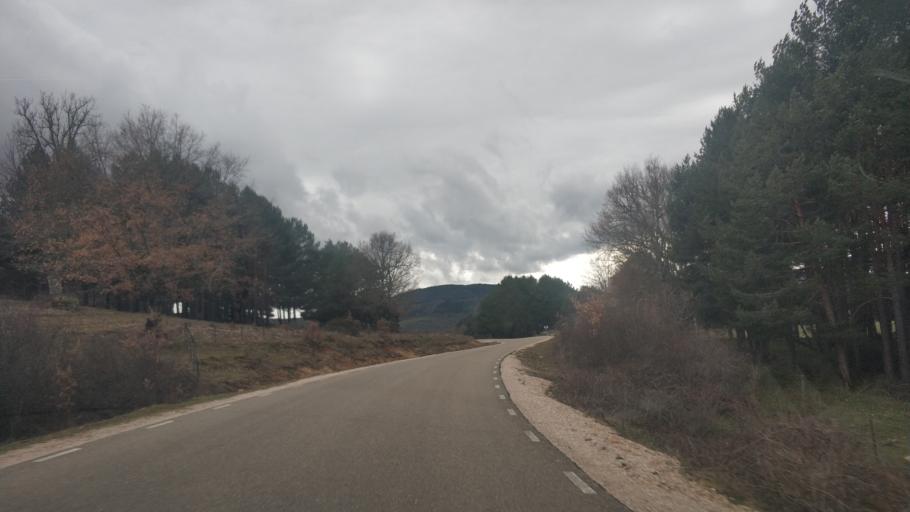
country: ES
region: Castille and Leon
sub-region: Provincia de Burgos
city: Canicosa de la Sierra
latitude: 41.9501
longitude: -3.0258
